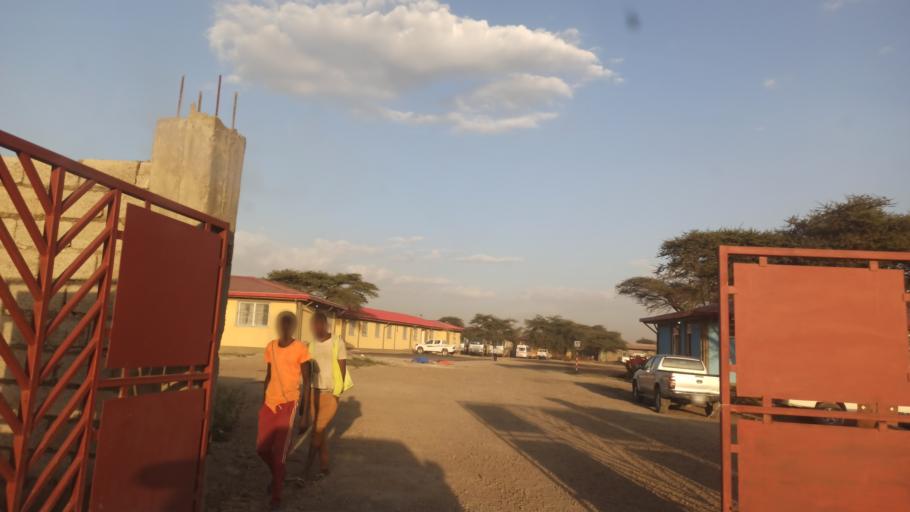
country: ET
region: Oromiya
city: Ziway
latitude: 7.7017
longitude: 38.6529
